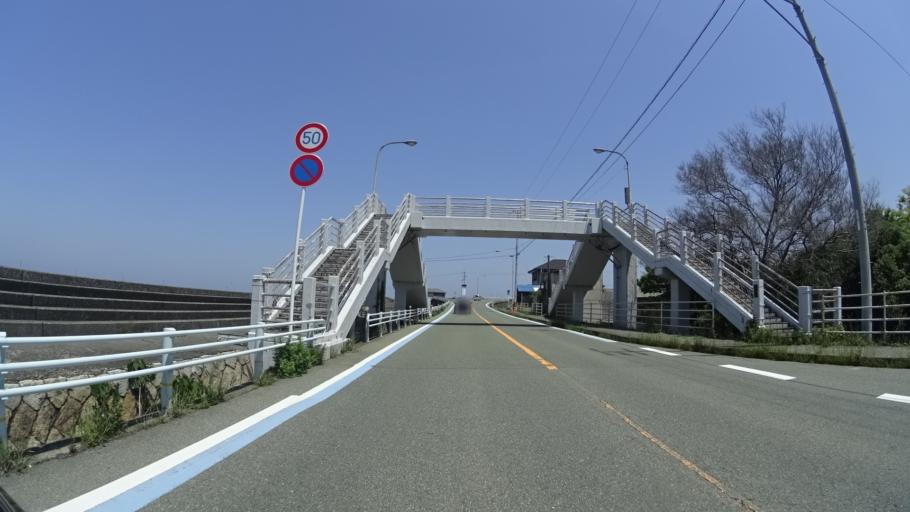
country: JP
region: Ehime
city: Ozu
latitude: 33.6089
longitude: 132.4754
